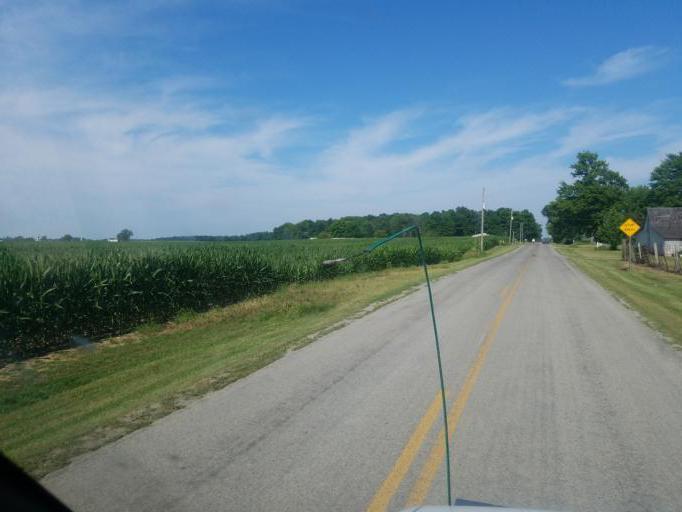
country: US
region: Ohio
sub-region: Logan County
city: Northwood
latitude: 40.5525
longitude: -83.6690
